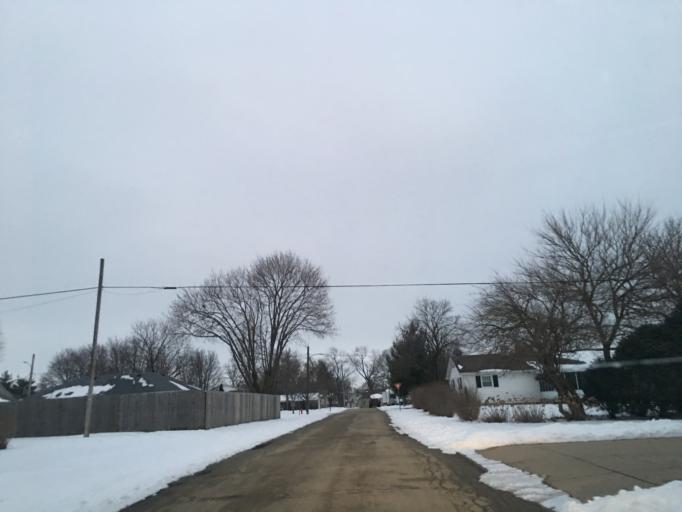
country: US
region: Illinois
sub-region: LaSalle County
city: Peru
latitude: 41.3328
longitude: -89.1358
